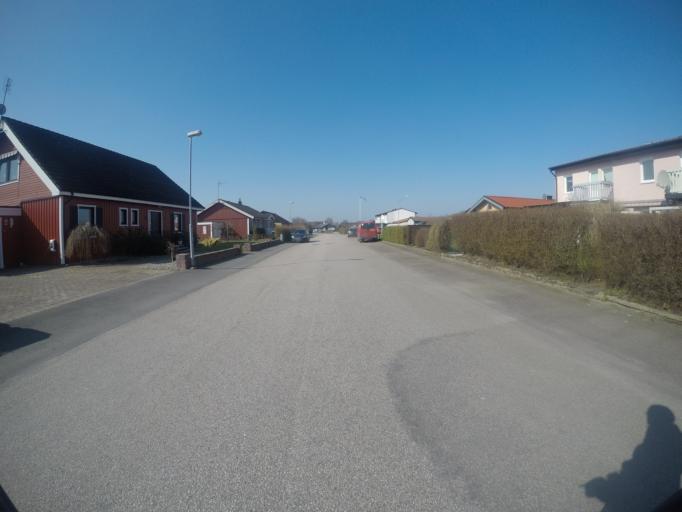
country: SE
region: Halland
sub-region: Laholms Kommun
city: Laholm
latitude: 56.5021
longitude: 13.0473
